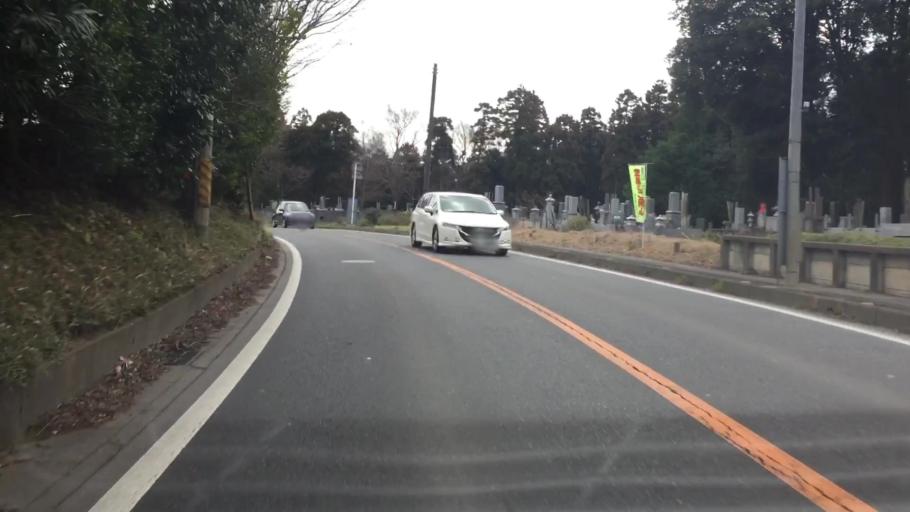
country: JP
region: Ibaraki
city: Ryugasaki
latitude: 35.8297
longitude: 140.1595
